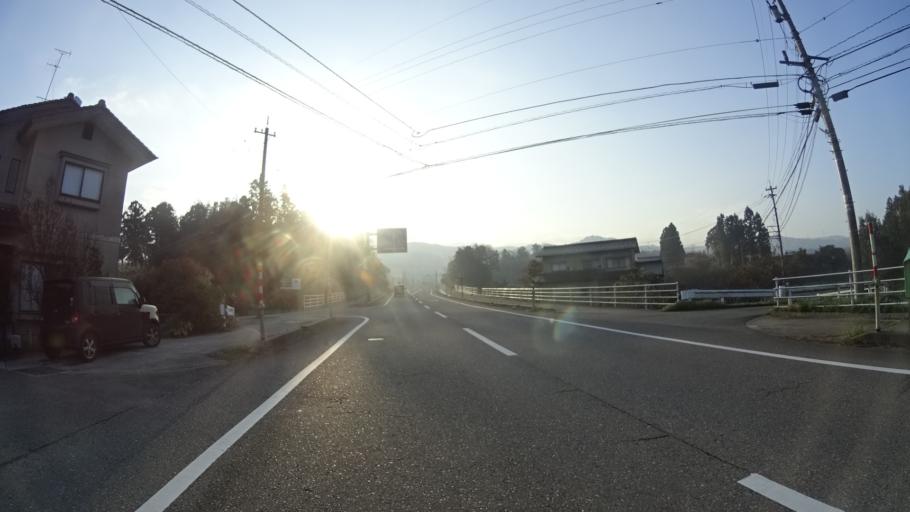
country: JP
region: Ishikawa
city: Nanao
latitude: 37.0271
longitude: 136.9750
